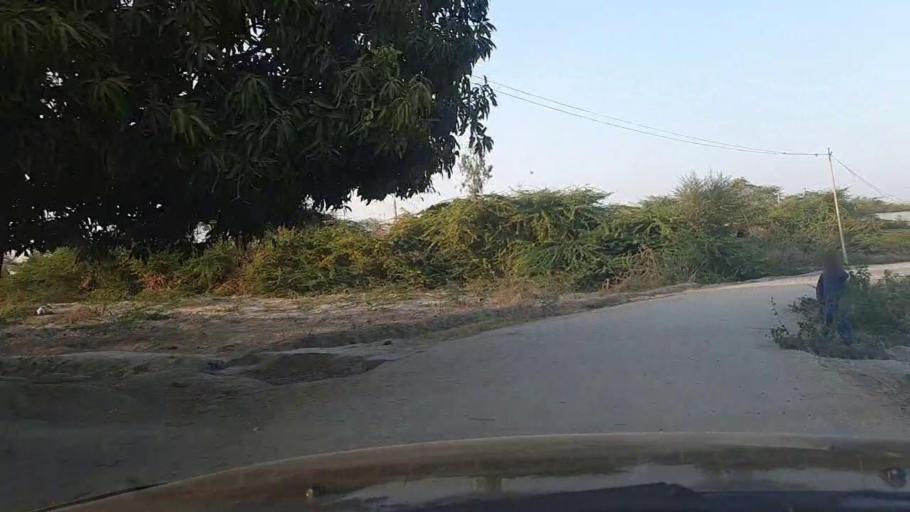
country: PK
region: Sindh
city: Naukot
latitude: 24.8668
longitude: 69.3228
